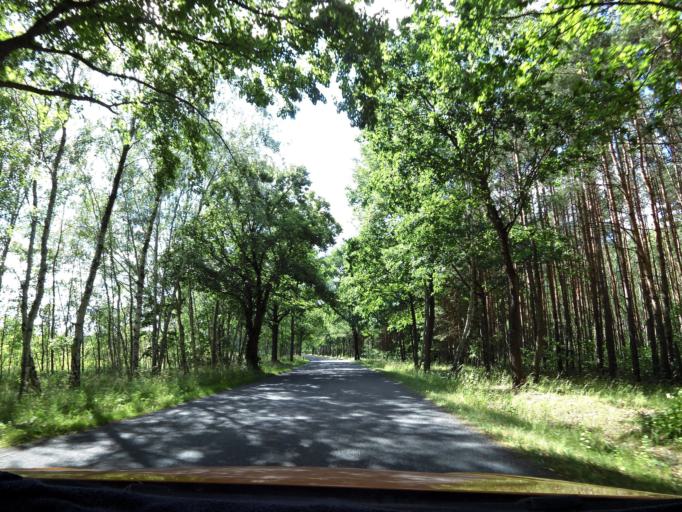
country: DE
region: Brandenburg
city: Erkner
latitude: 52.3190
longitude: 13.7643
